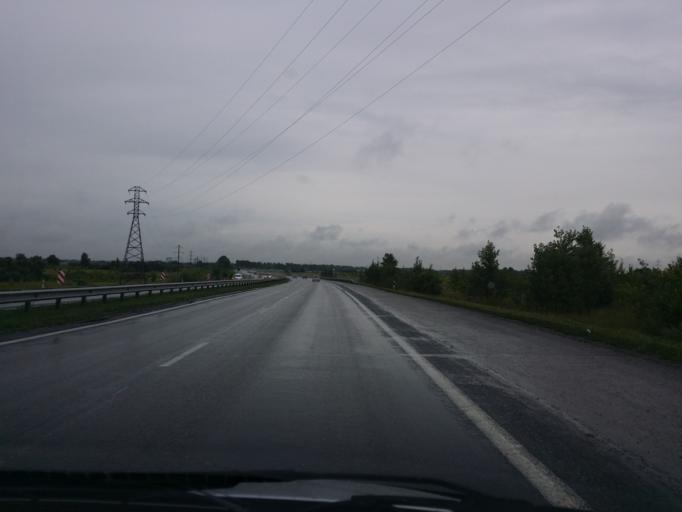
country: RU
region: Altai Krai
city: Sannikovo
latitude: 53.3551
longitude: 83.9491
